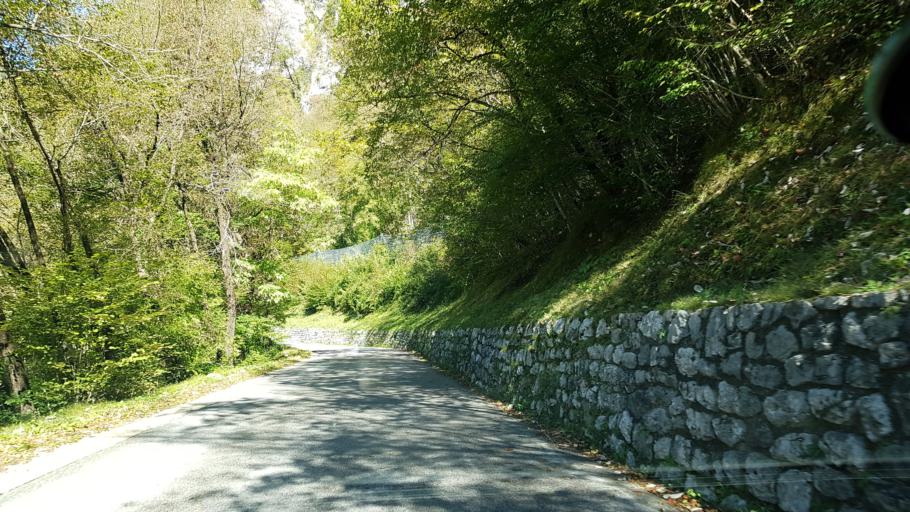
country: SI
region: Kobarid
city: Kobarid
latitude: 46.2510
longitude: 13.5955
